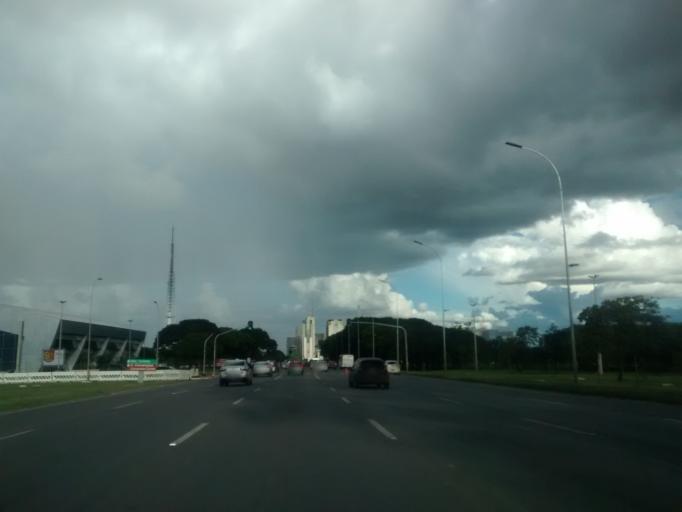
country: BR
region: Federal District
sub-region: Brasilia
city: Brasilia
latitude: -15.7895
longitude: -47.9027
